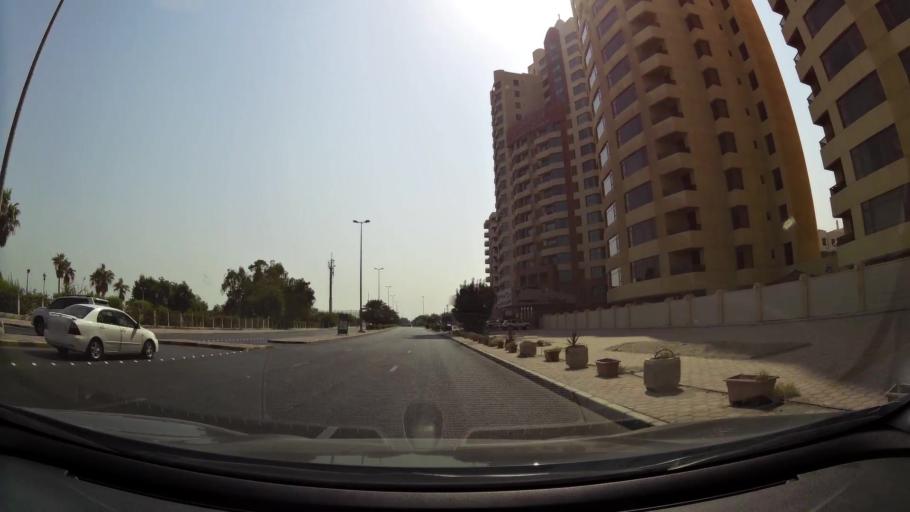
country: KW
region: Al Ahmadi
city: Al Fintas
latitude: 29.1819
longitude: 48.1189
